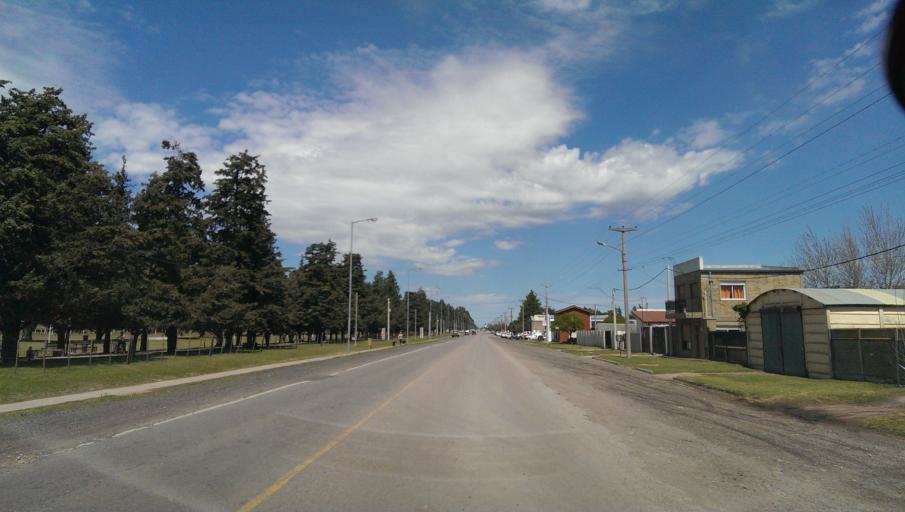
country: AR
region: Buenos Aires
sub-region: Partido de Tornquist
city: Tornquist
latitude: -38.0913
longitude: -62.2189
